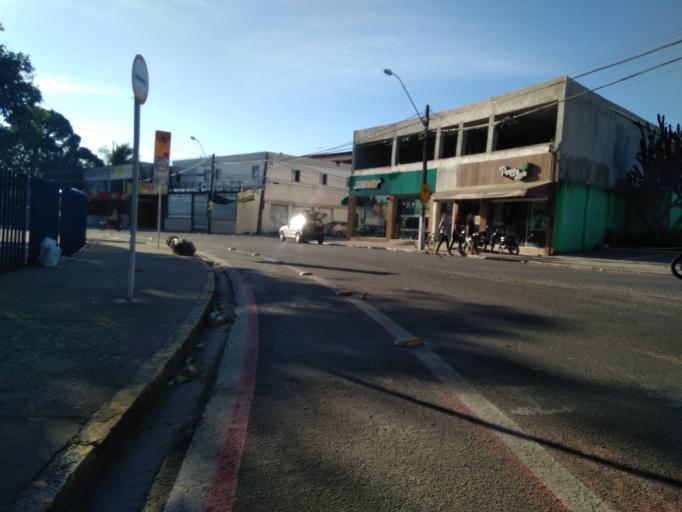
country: BR
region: Pernambuco
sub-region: Recife
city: Recife
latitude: -8.0815
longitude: -34.9379
